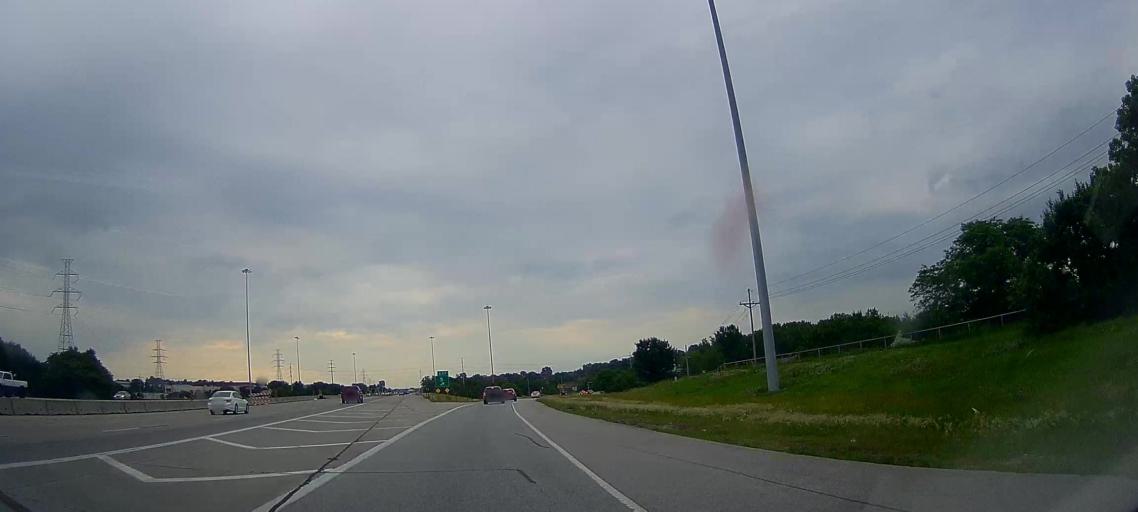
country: US
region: Nebraska
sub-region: Douglas County
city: Ralston
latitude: 41.3036
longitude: -96.0706
